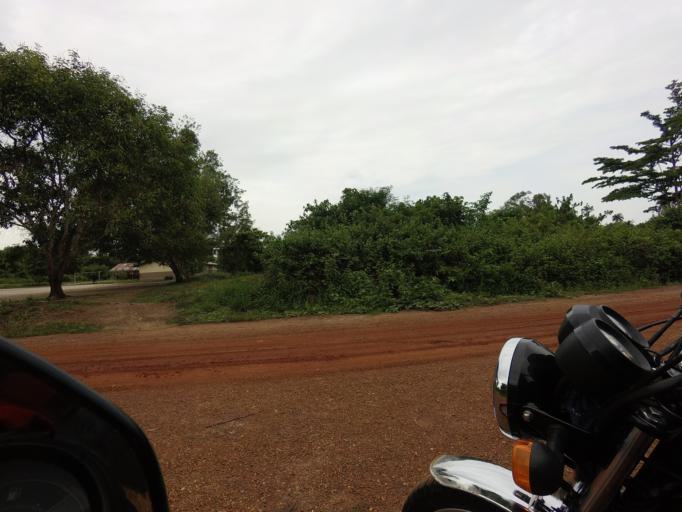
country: SL
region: Eastern Province
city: Mobai
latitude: 7.9936
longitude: -10.7230
